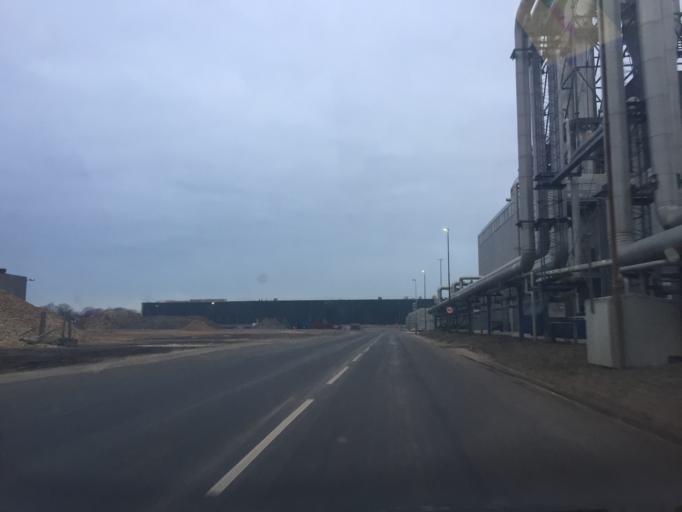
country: DK
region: Zealand
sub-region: Koge Kommune
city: Koge
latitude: 55.4625
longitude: 12.1920
